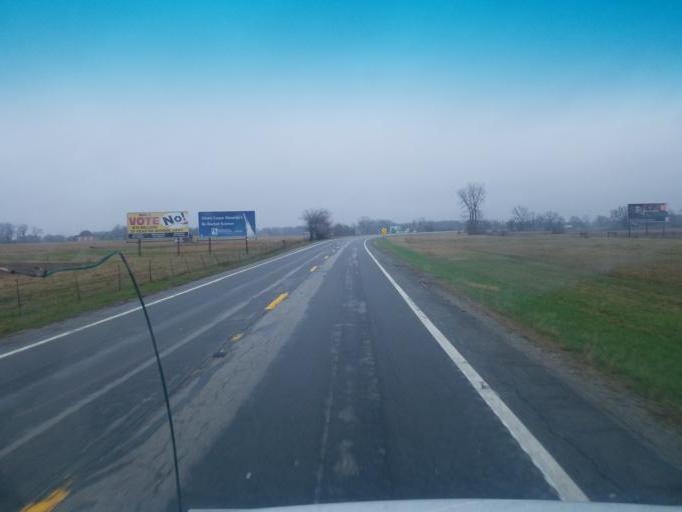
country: US
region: Ohio
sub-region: Wood County
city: Bowling Green
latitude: 41.3721
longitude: -83.7183
